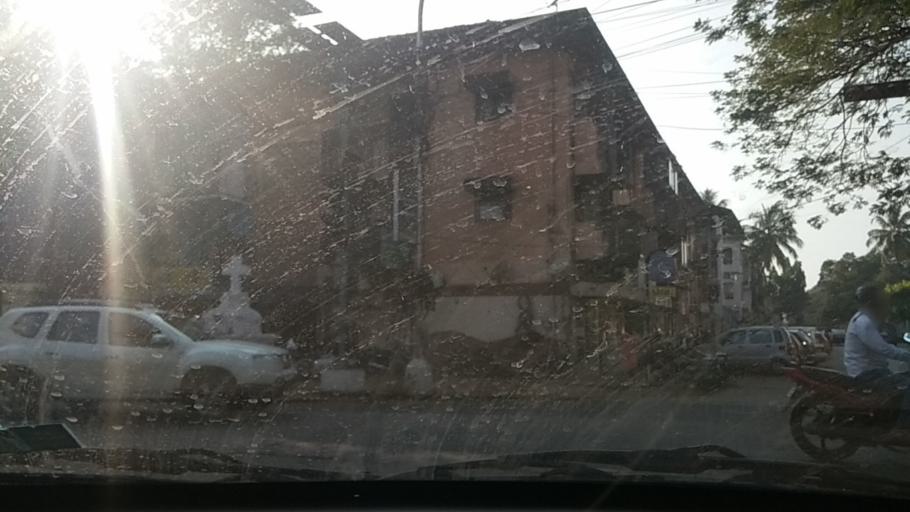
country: IN
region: Goa
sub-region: North Goa
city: Panaji
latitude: 15.4933
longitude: 73.8207
